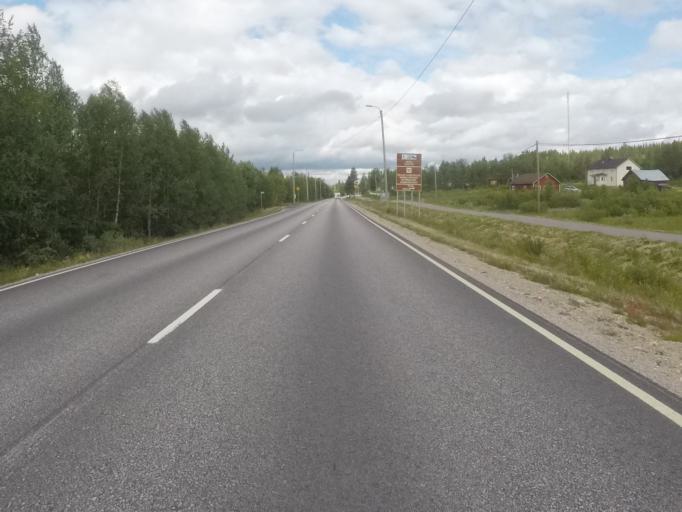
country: FI
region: Lapland
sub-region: Tunturi-Lappi
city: Enontekioe
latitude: 68.2782
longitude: 23.0869
